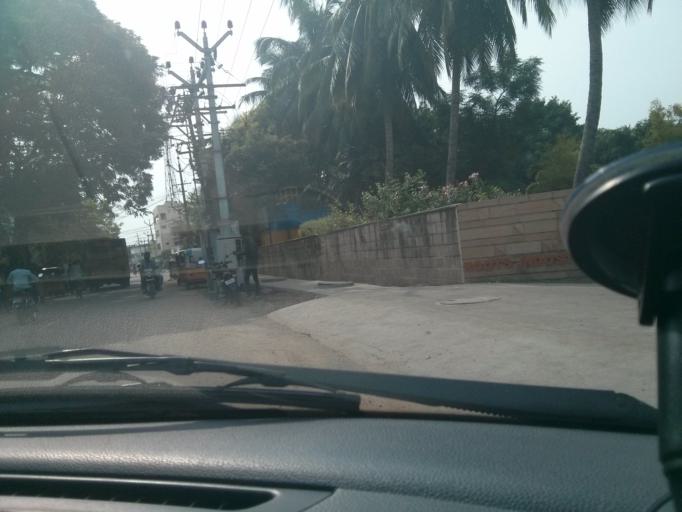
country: IN
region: Tamil Nadu
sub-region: Coimbatore
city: Coimbatore
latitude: 11.0344
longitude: 76.9672
